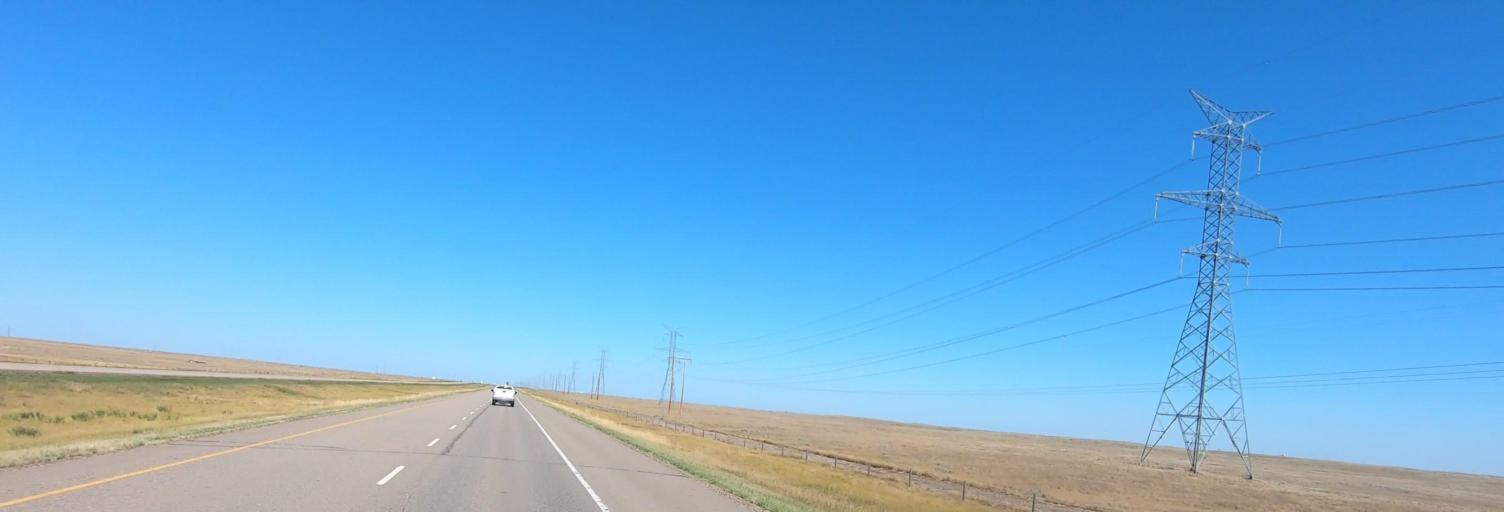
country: CA
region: Alberta
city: Brooks
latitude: 50.3847
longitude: -111.4597
